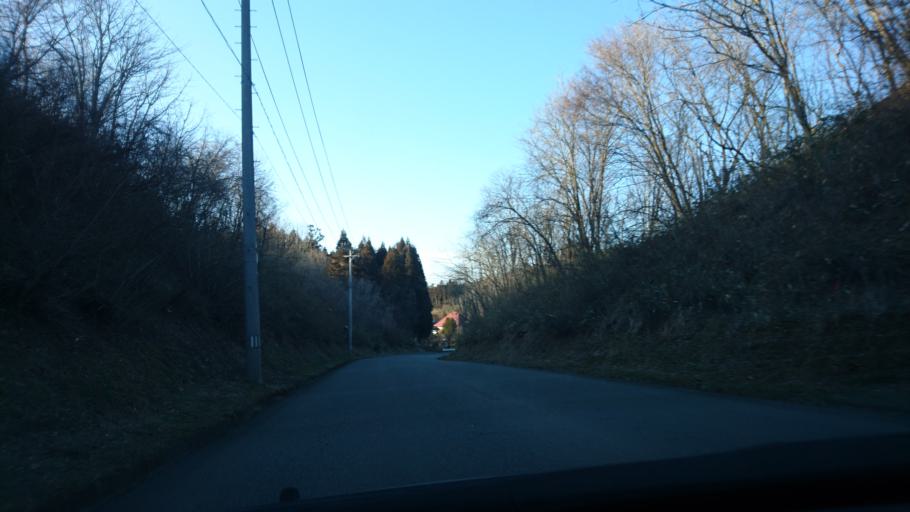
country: JP
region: Iwate
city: Ichinoseki
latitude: 38.9396
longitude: 141.3605
